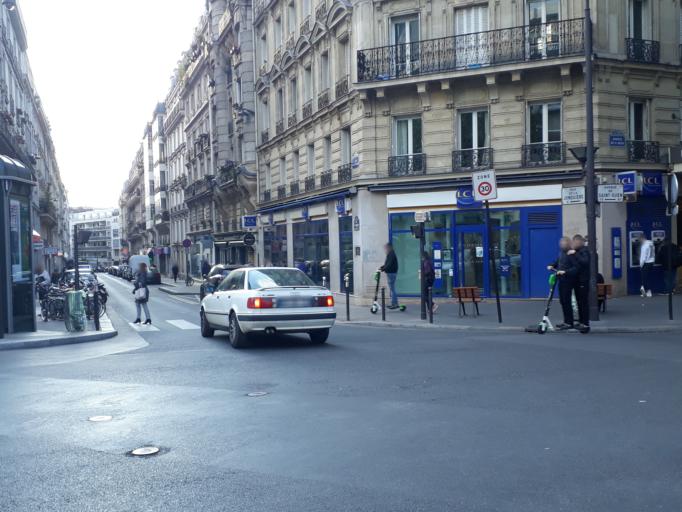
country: FR
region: Ile-de-France
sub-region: Paris
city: Saint-Ouen
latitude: 48.8930
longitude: 2.3274
